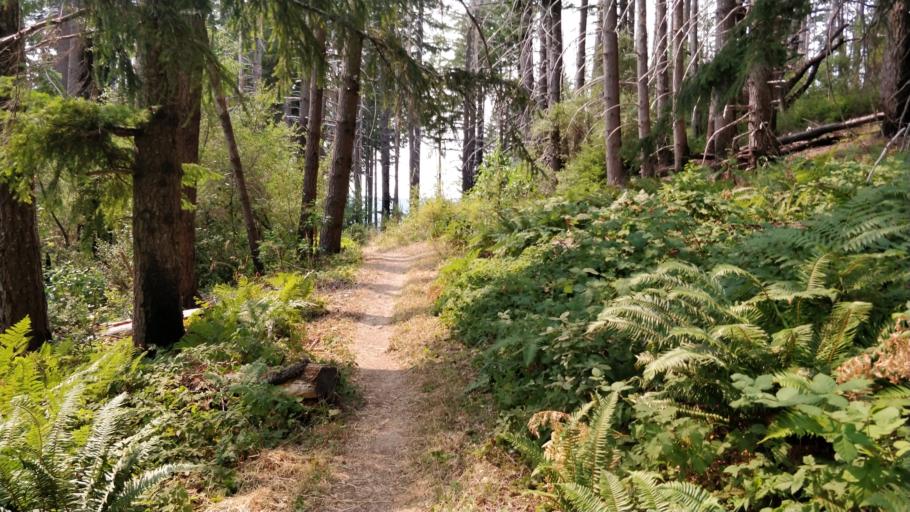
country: US
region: California
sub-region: Humboldt County
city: Westhaven-Moonstone
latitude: 41.2026
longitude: -123.9491
